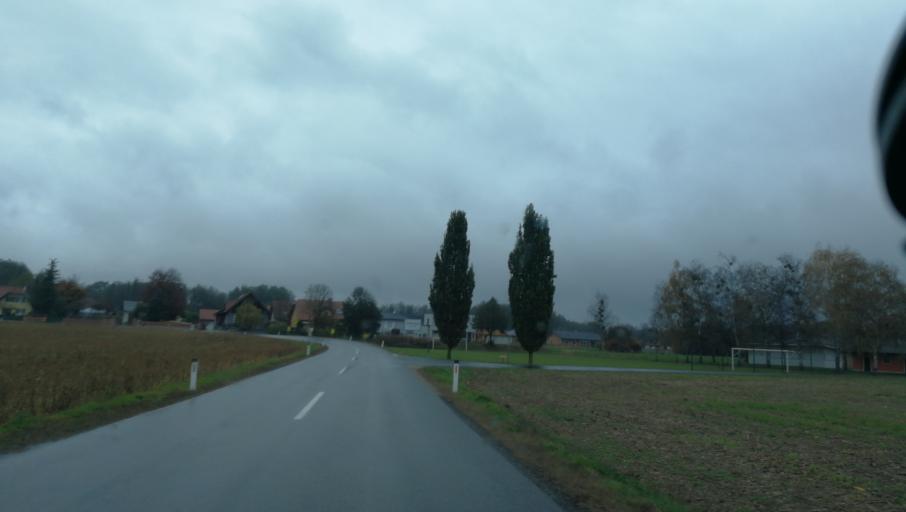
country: AT
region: Styria
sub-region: Politischer Bezirk Leibnitz
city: Spielfeld
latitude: 46.7302
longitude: 15.6648
